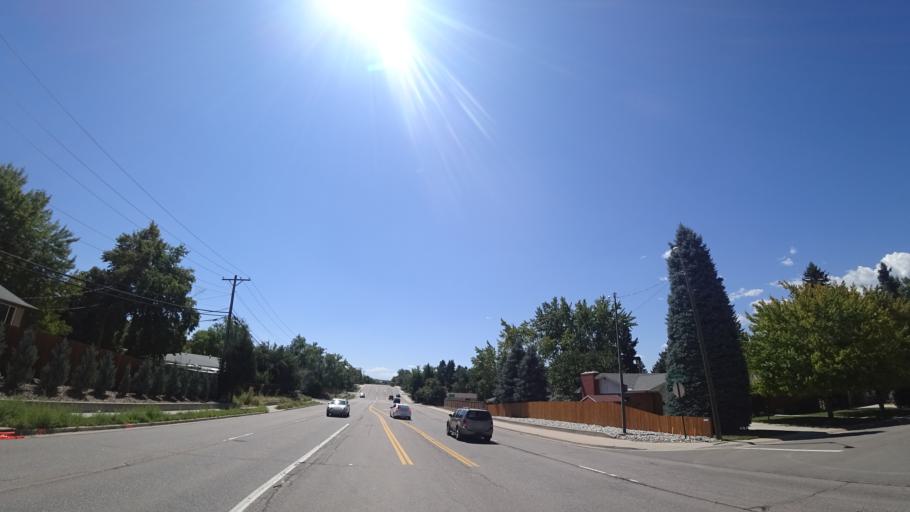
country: US
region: Colorado
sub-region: Arapahoe County
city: Greenwood Village
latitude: 39.6072
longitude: -104.9600
